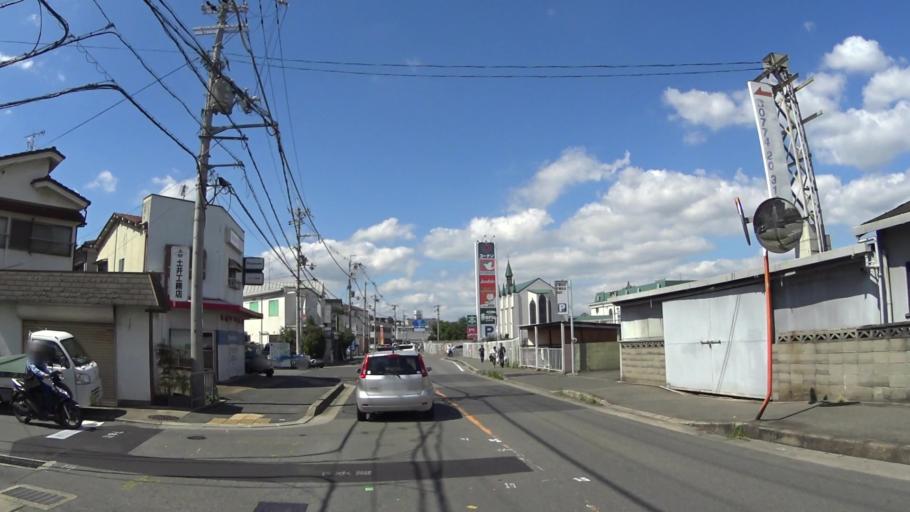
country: JP
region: Kyoto
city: Uji
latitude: 34.8910
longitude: 135.7950
